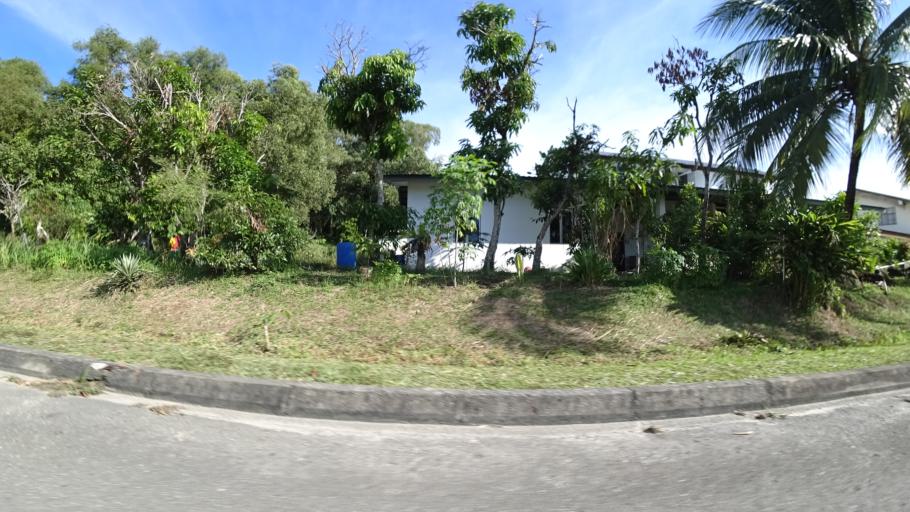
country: BN
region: Brunei and Muara
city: Bandar Seri Begawan
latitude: 4.9780
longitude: 114.9796
